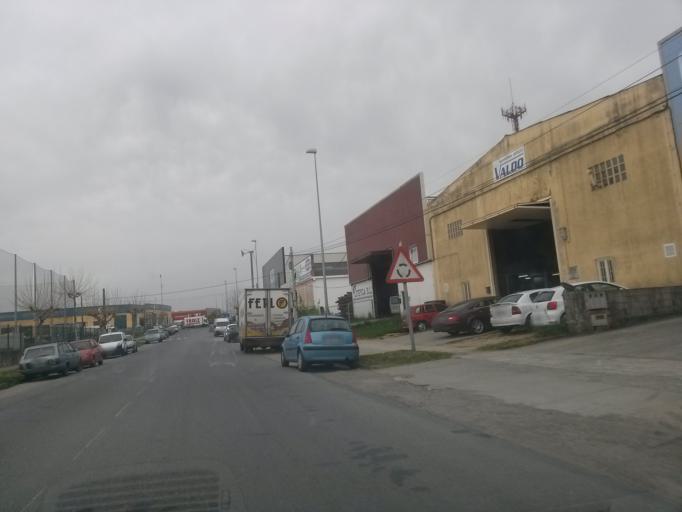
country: ES
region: Galicia
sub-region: Provincia de Lugo
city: Lugo
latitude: 43.0484
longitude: -7.5702
